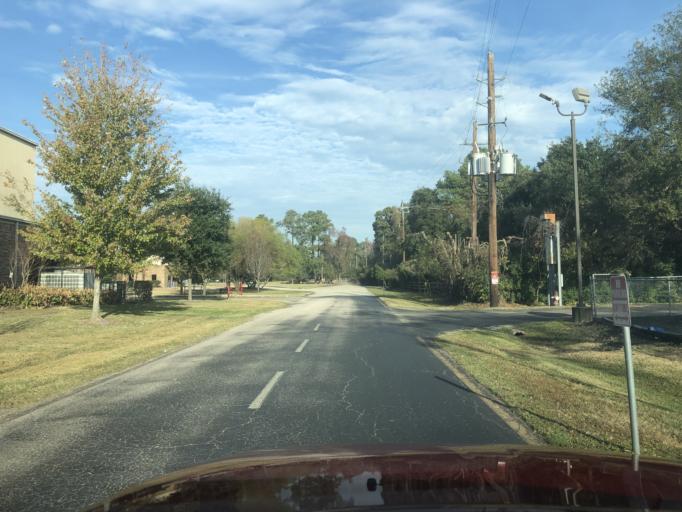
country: US
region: Texas
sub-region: Harris County
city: Spring
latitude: 30.0050
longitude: -95.4704
